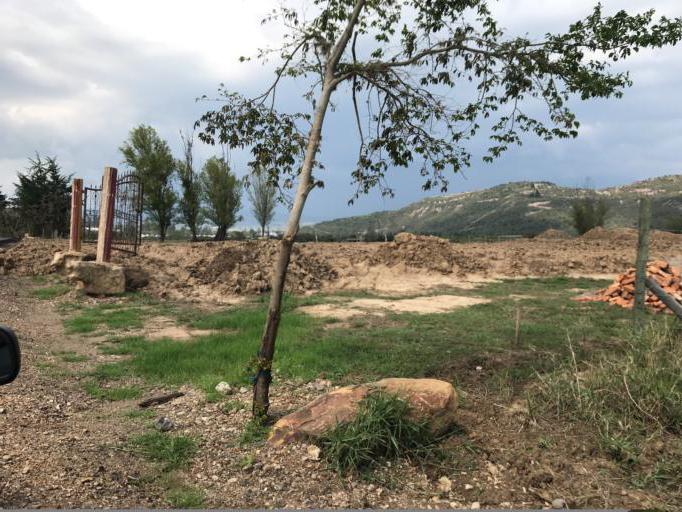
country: CO
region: Boyaca
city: Sutamarchan
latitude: 5.6383
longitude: -73.5984
